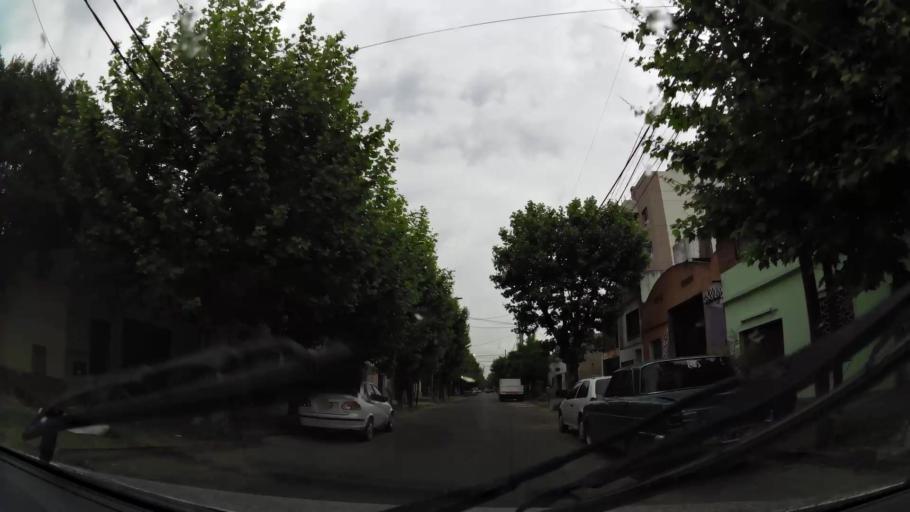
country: AR
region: Buenos Aires
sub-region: Partido de Lanus
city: Lanus
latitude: -34.7009
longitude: -58.3992
